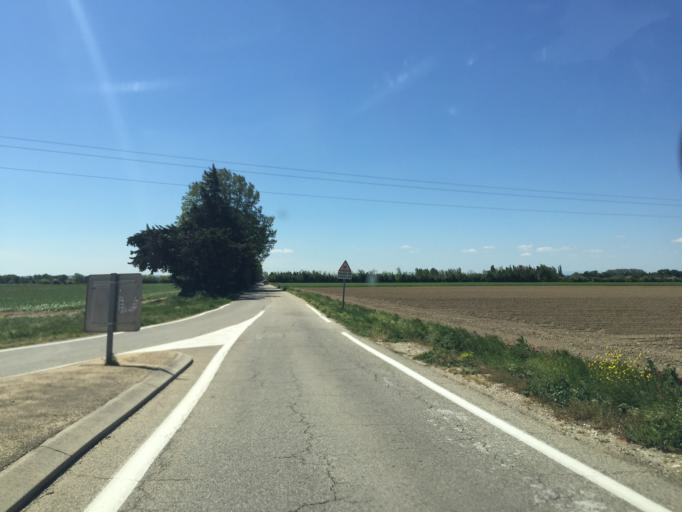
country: FR
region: Provence-Alpes-Cote d'Azur
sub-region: Departement du Vaucluse
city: Jonquieres
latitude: 44.1259
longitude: 4.9334
